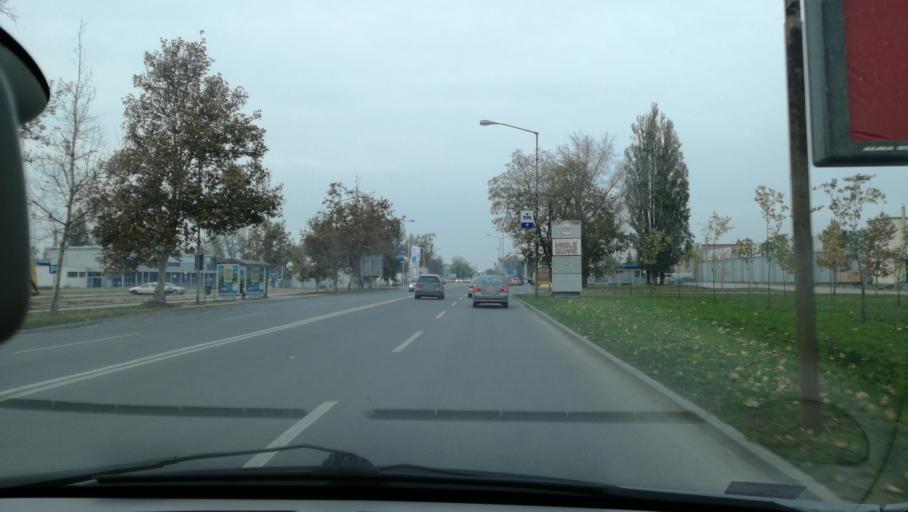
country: RS
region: Autonomna Pokrajina Vojvodina
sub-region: Juznobacki Okrug
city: Novi Sad
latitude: 45.2709
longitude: 19.8312
